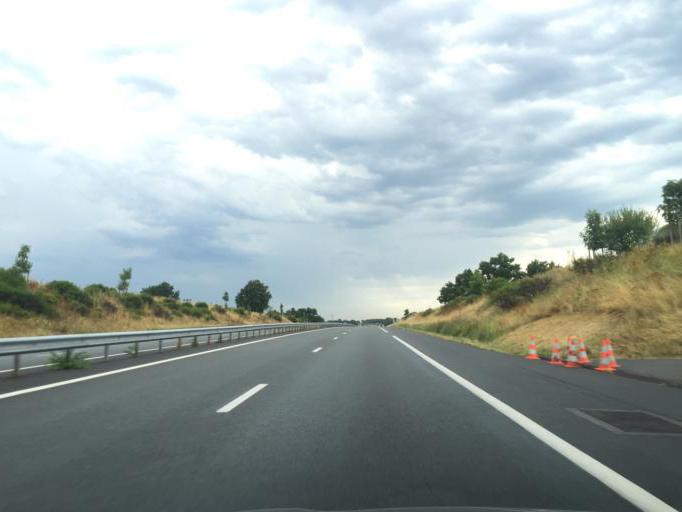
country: FR
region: Rhone-Alpes
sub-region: Departement de la Loire
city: La Pacaudiere
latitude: 46.1614
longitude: 3.8898
